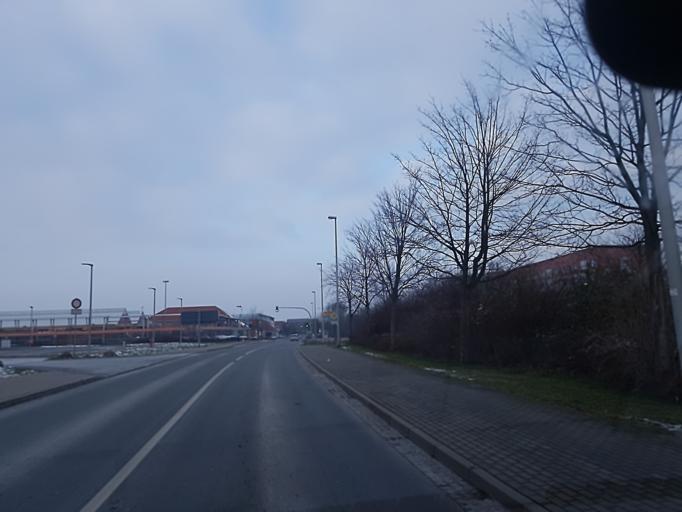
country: DE
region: Saxony
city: Oschatz
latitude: 51.2966
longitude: 13.0956
